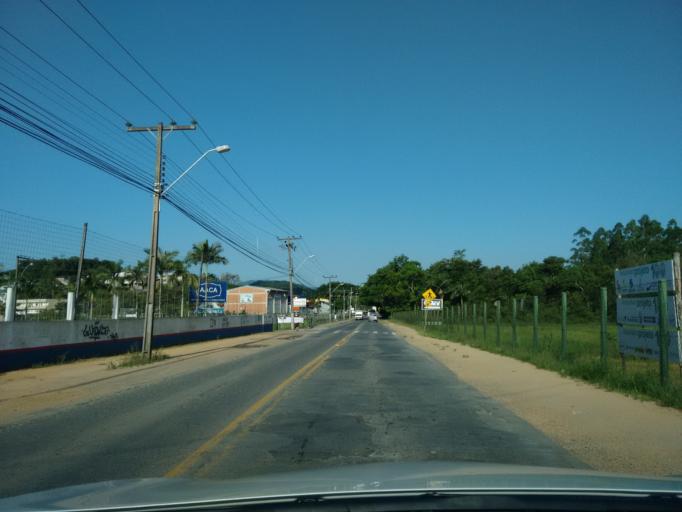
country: BR
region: Santa Catarina
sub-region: Blumenau
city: Blumenau
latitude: -26.8501
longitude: -49.0857
